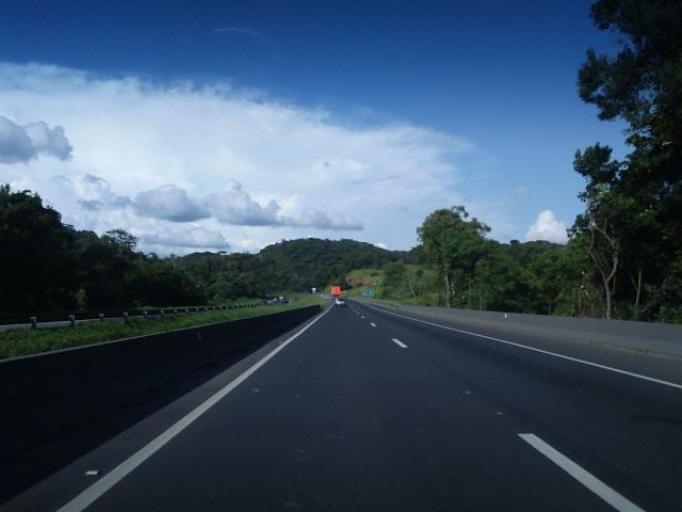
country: BR
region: Sao Paulo
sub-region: Miracatu
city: Miracatu
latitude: -24.2434
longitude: -47.3651
